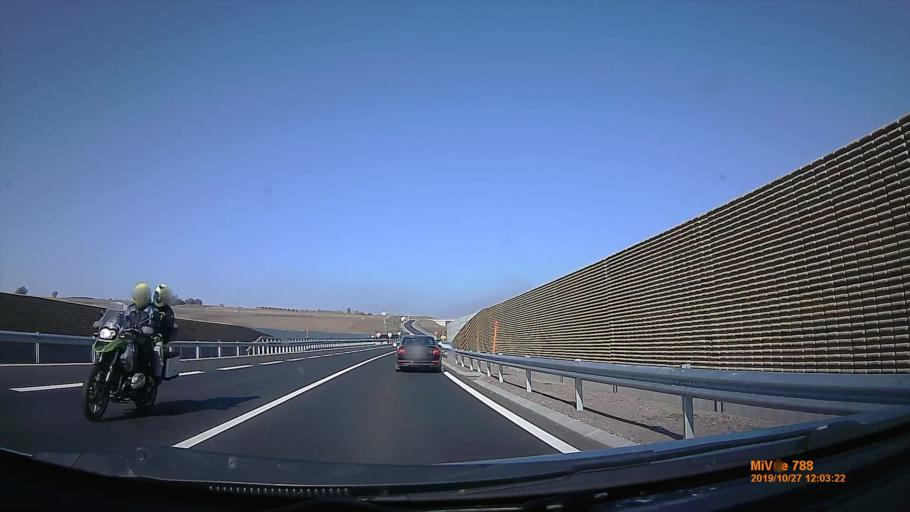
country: AT
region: Lower Austria
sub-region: Politischer Bezirk Mistelbach
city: Drasenhofen
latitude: 48.7418
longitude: 16.6379
